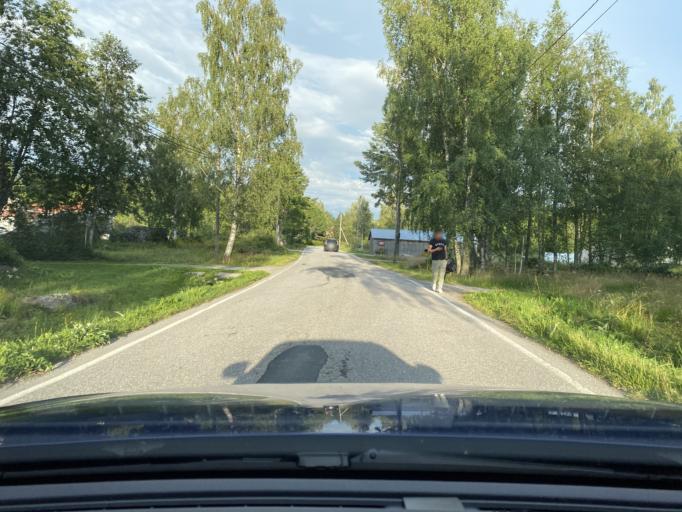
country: FI
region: Ostrobothnia
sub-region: Vaasa
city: Korsnaes
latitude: 62.9719
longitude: 21.1807
